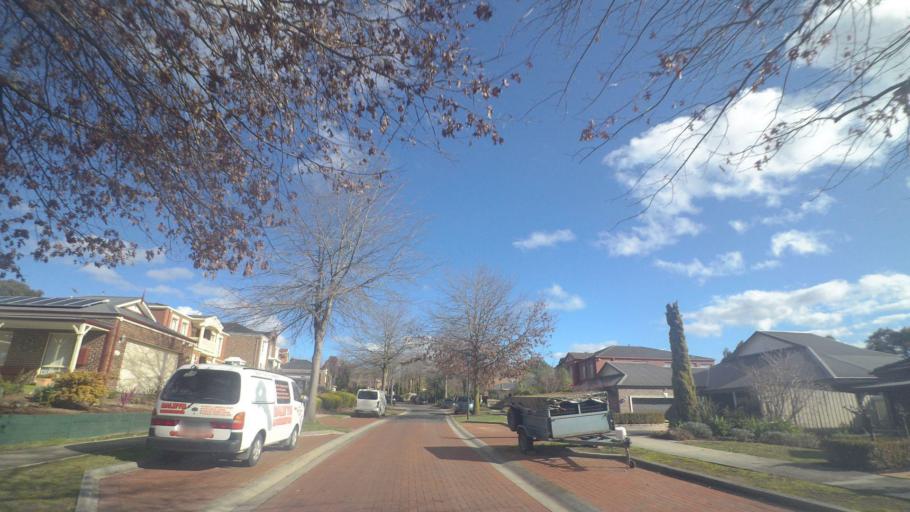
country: AU
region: Victoria
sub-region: Yarra Ranges
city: Lysterfield
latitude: -37.9222
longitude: 145.2796
